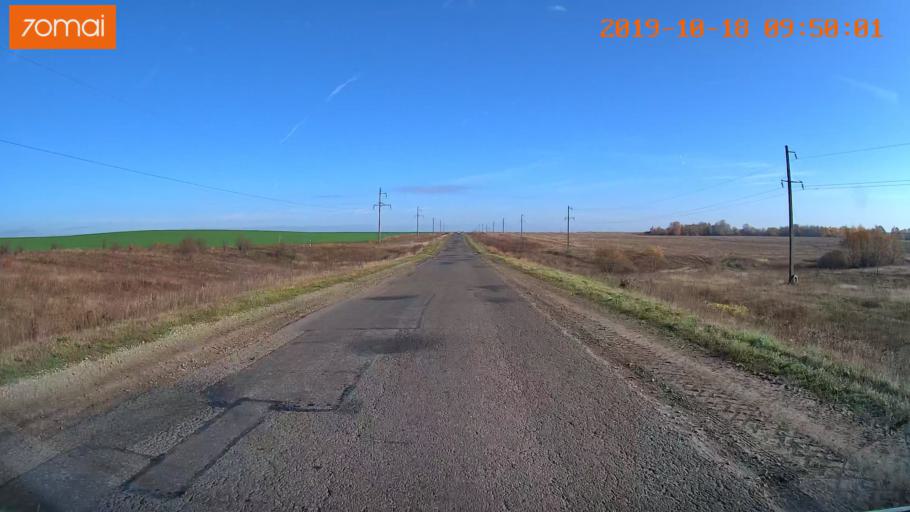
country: RU
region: Tula
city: Kazachka
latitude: 53.3242
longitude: 38.2715
